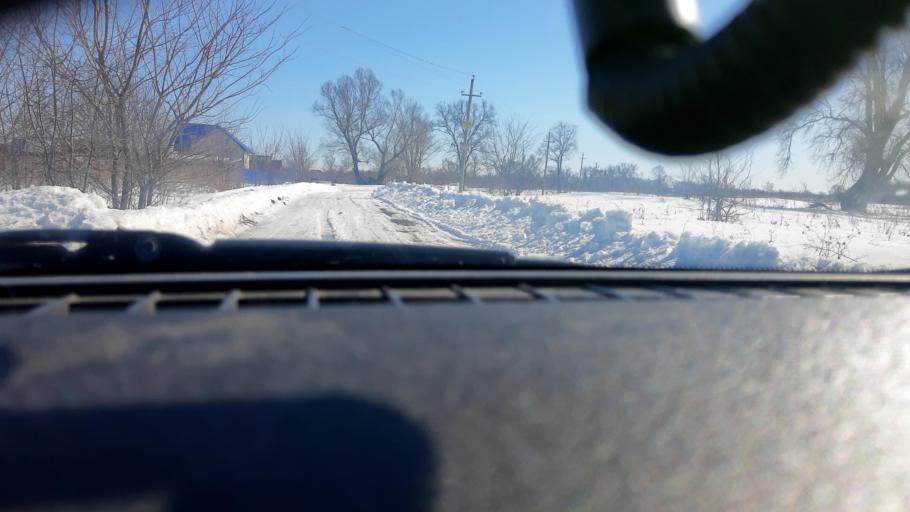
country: RU
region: Bashkortostan
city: Ufa
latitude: 54.7758
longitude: 56.1916
